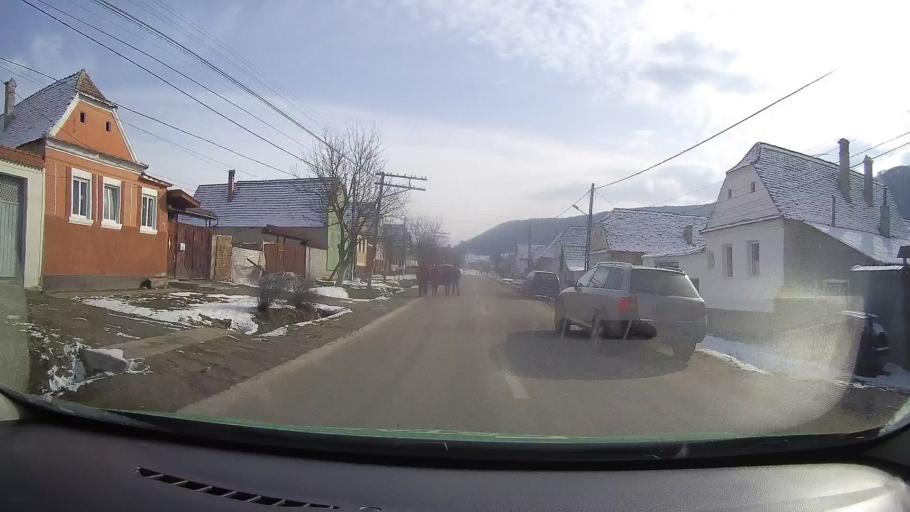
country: RO
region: Mures
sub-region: Comuna Apold
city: Saes
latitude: 46.1539
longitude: 24.7700
